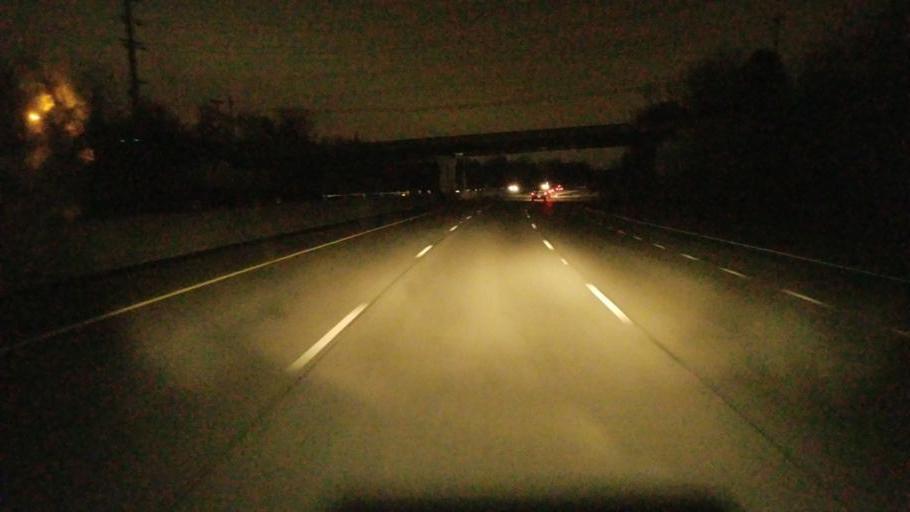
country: US
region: Ohio
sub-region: Franklin County
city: Huber Ridge
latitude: 40.0799
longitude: -82.8659
